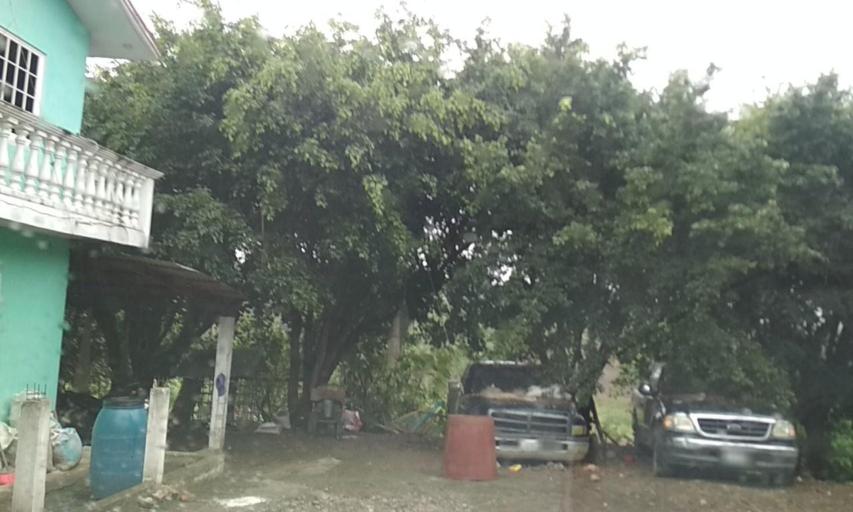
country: MX
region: Puebla
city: Espinal
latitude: 20.3286
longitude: -97.3938
